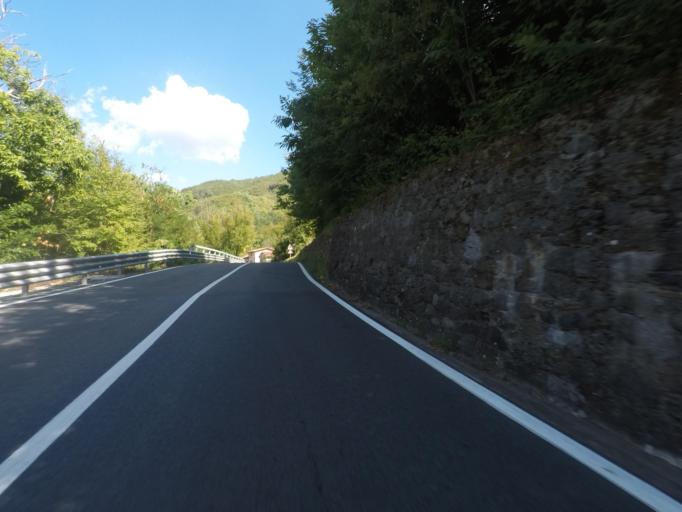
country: IT
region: Tuscany
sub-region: Provincia di Massa-Carrara
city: Fivizzano
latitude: 44.2446
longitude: 10.1625
